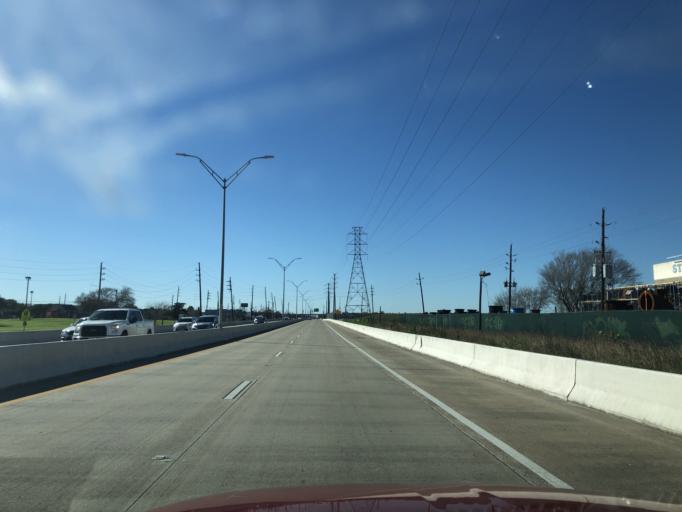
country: US
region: Texas
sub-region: Fort Bend County
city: Mission Bend
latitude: 29.7121
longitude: -95.6311
